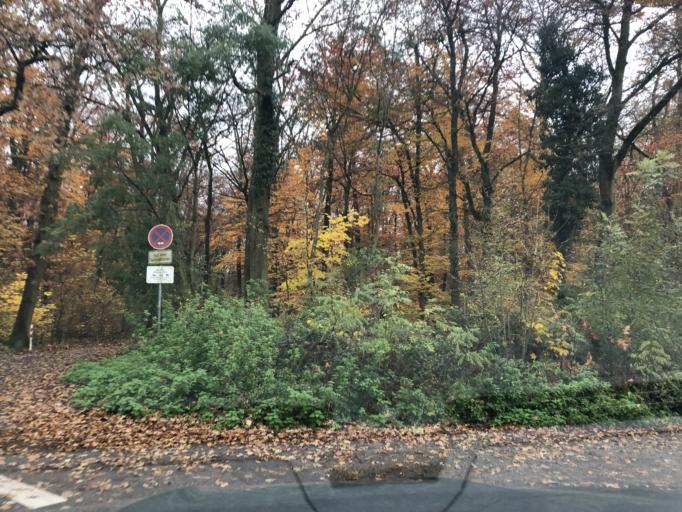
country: DE
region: Baden-Wuerttemberg
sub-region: Karlsruhe Region
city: Walldorf
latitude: 49.2849
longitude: 8.6484
